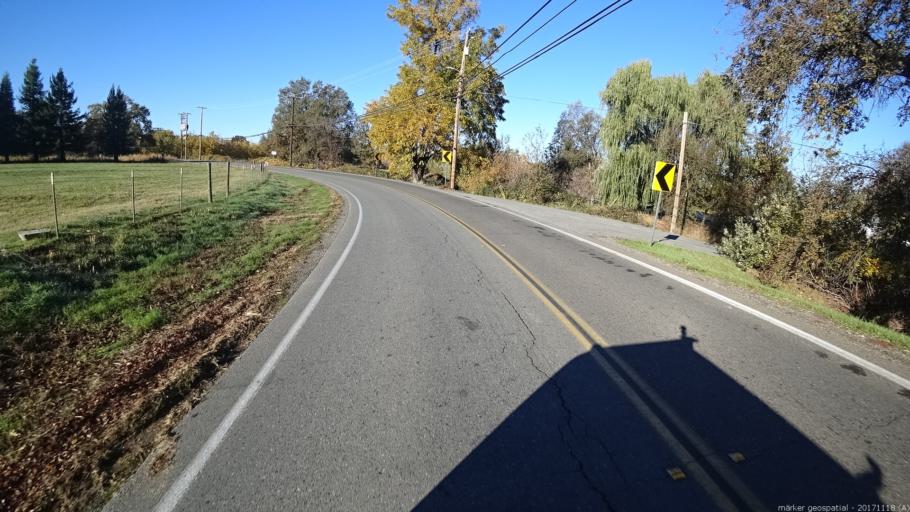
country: US
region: California
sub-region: Shasta County
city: Anderson
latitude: 40.4552
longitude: -122.2738
